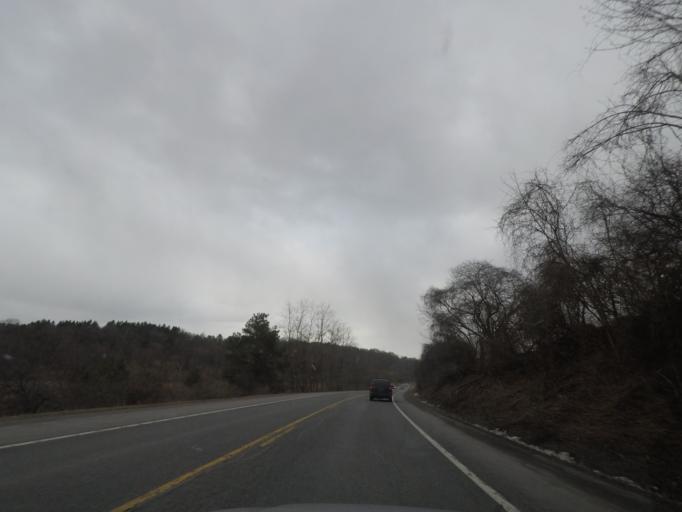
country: US
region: New York
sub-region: Onondaga County
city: Manlius
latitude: 43.0440
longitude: -75.9575
